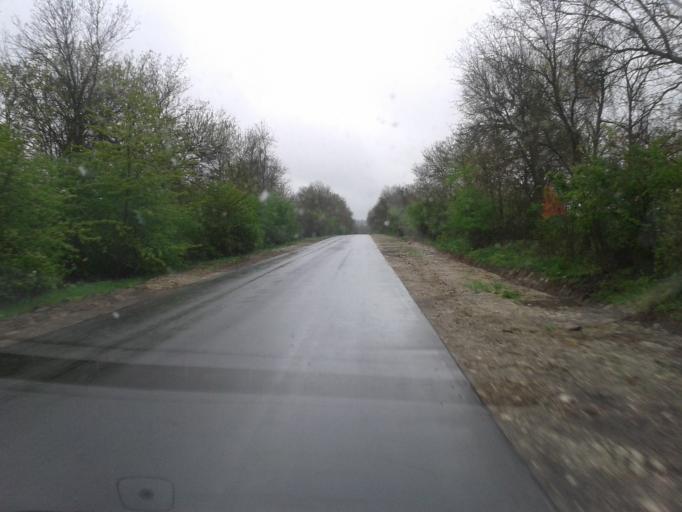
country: PL
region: Lublin Voivodeship
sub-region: Powiat tomaszowski
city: Jarczow
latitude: 50.3644
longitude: 23.6034
